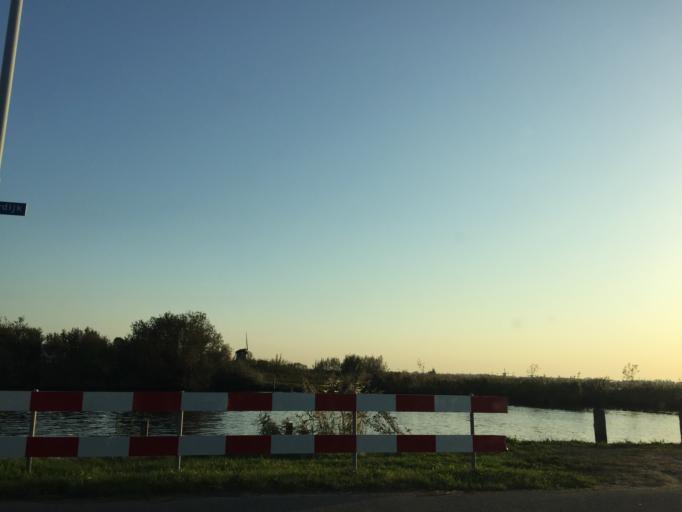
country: NL
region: South Holland
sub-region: Gemeente Kaag en Braassem
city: Oude Wetering
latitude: 52.2151
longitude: 4.6030
